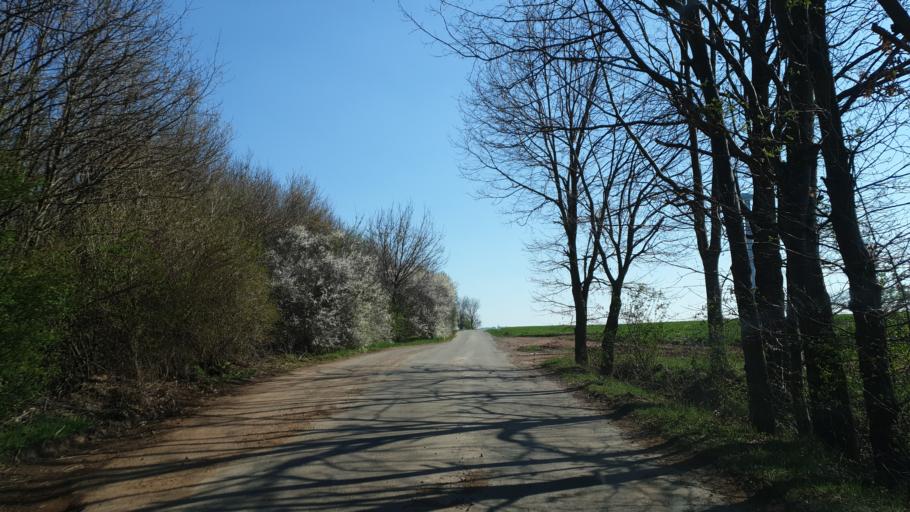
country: DE
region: Saxony
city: Hohndorf
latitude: 50.7590
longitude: 12.6855
